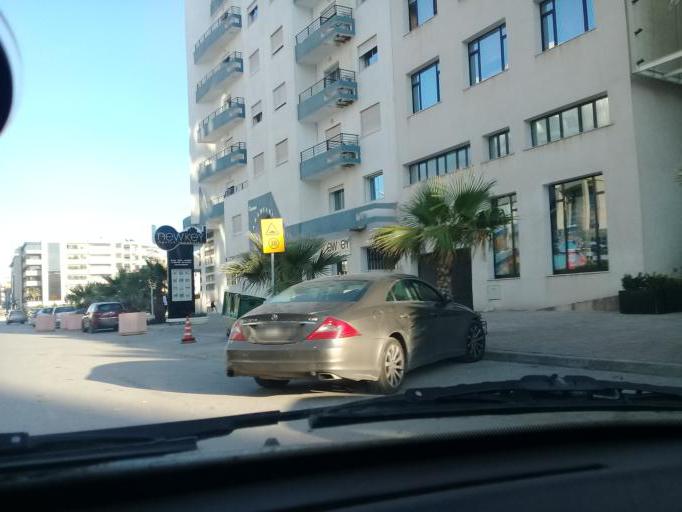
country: TN
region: Tunis
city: La Goulette
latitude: 36.8472
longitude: 10.2775
